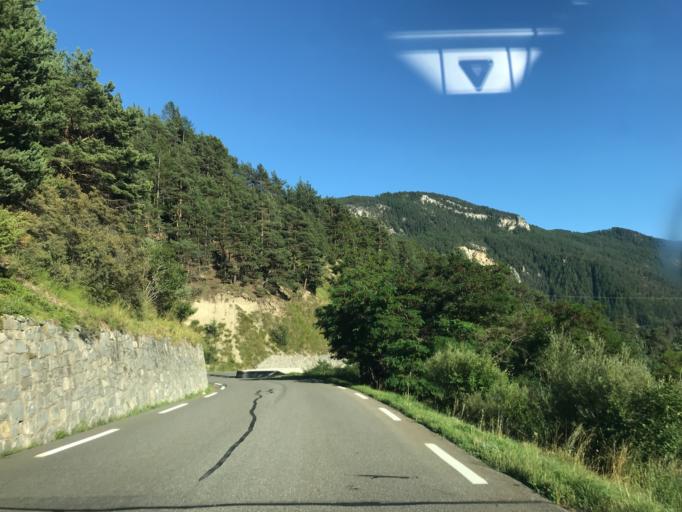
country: FR
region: Provence-Alpes-Cote d'Azur
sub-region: Departement des Hautes-Alpes
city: Guillestre
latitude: 44.7504
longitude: 6.7653
